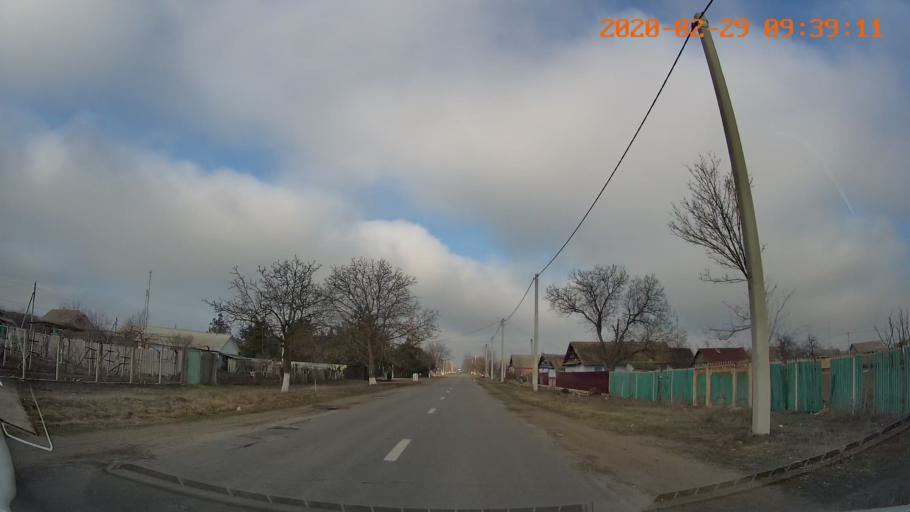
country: MD
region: Telenesti
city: Crasnoe
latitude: 46.6343
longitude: 29.8577
